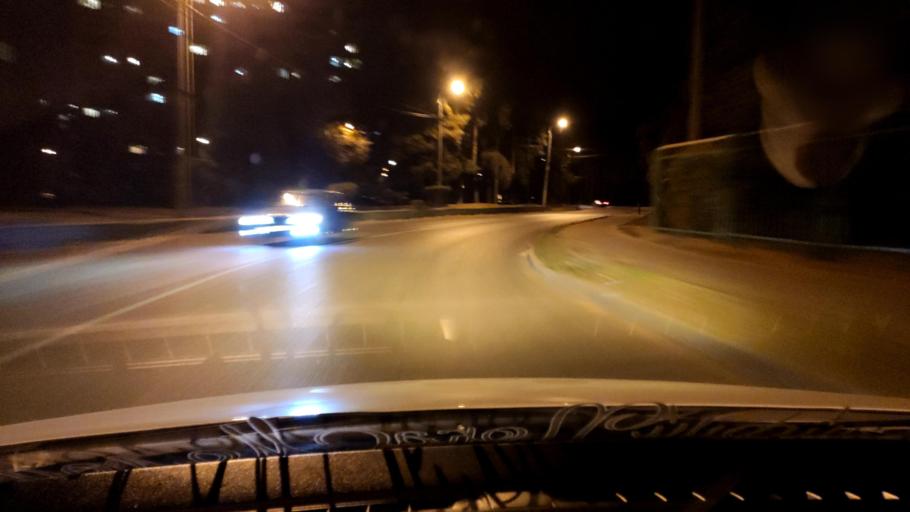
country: RU
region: Voronezj
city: Pridonskoy
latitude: 51.6860
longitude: 39.0801
